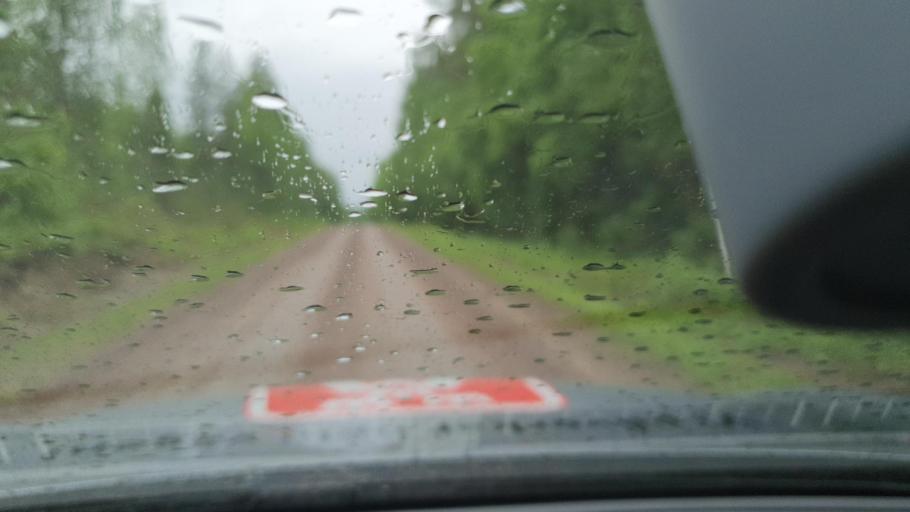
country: SE
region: Norrbotten
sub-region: Overkalix Kommun
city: OEverkalix
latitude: 66.5291
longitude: 22.7411
